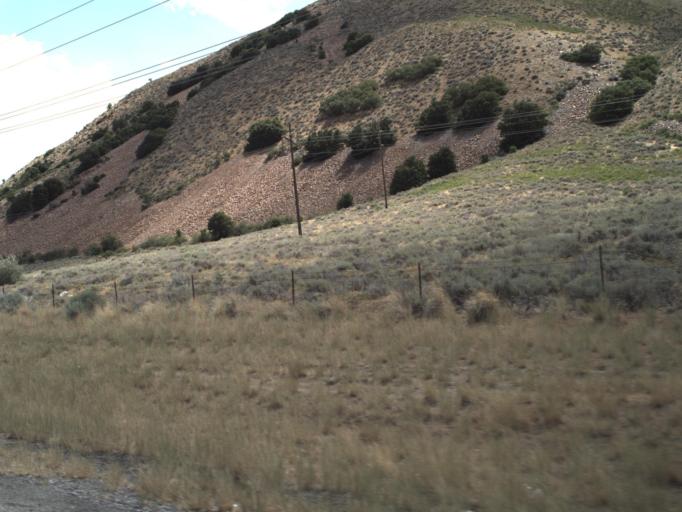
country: US
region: Utah
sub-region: Tooele County
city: Tooele
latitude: 40.5093
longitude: -112.3154
